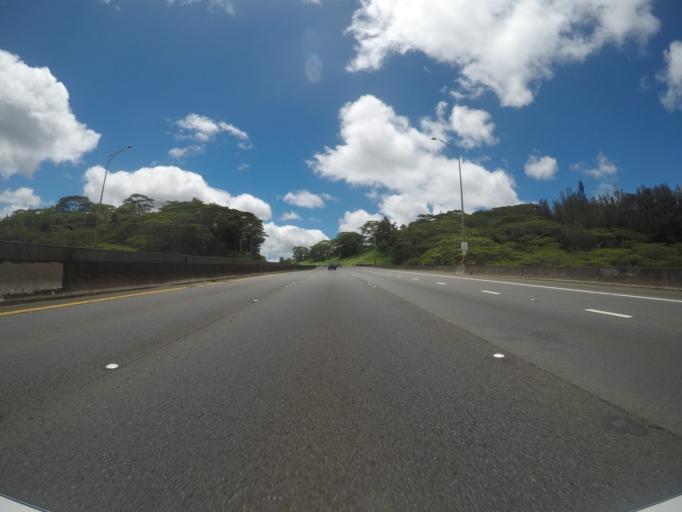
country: US
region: Hawaii
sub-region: Honolulu County
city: Mililani Town
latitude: 21.4600
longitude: -157.9945
